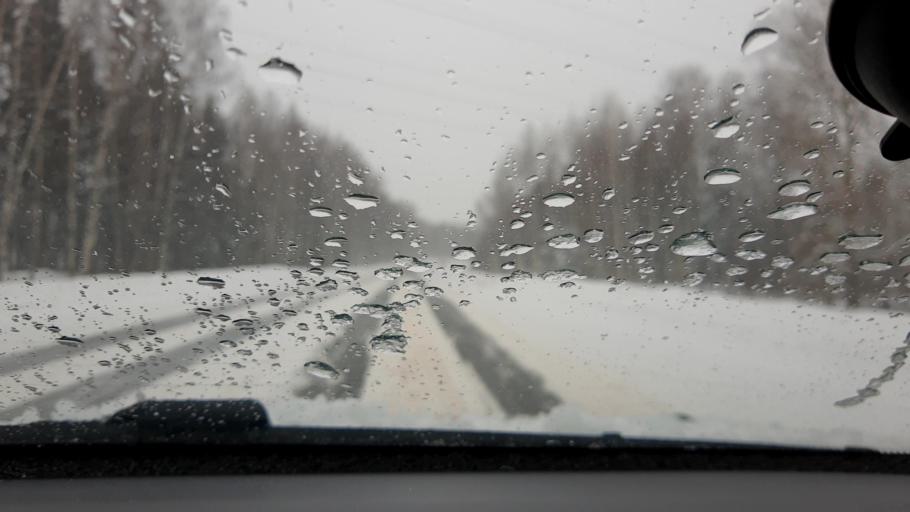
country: RU
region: Nizjnij Novgorod
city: Pervomayskiy
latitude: 56.6289
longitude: 43.2445
